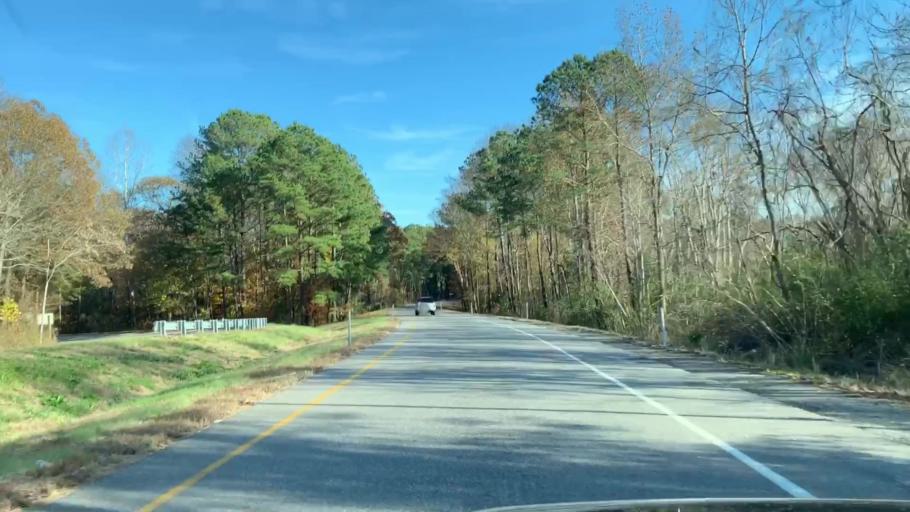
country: US
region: Virginia
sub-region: James City County
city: Williamsburg
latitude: 37.3831
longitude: -76.7633
